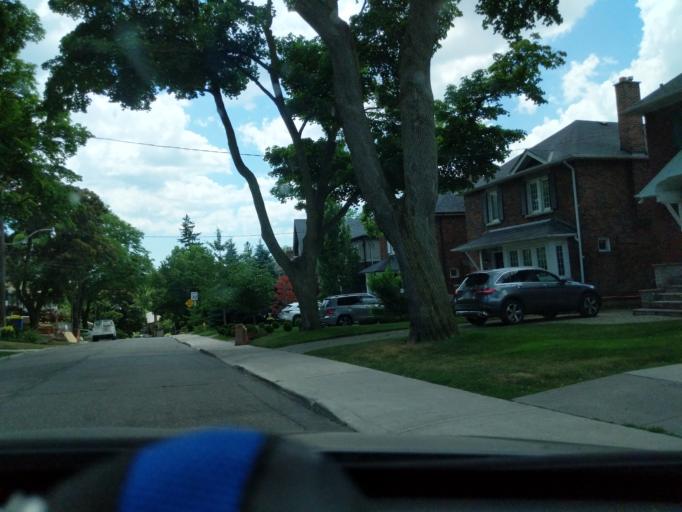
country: CA
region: Ontario
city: Toronto
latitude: 43.7028
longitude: -79.4142
